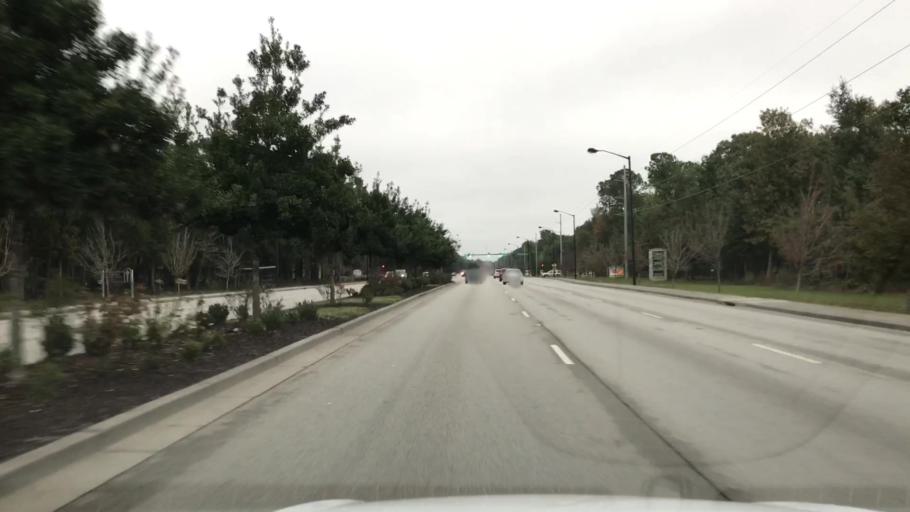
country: US
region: South Carolina
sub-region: Charleston County
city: Isle of Palms
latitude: 32.8635
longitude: -79.7886
